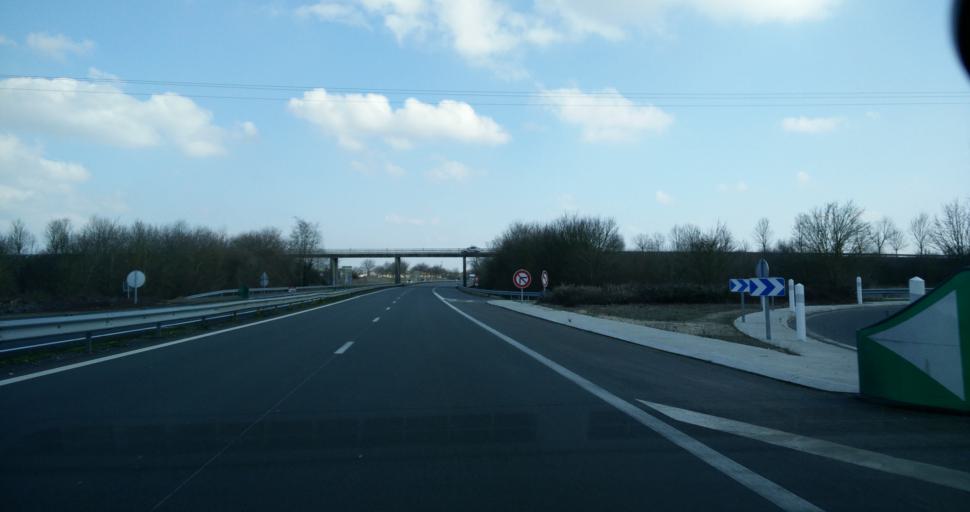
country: FR
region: Poitou-Charentes
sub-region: Departement de la Charente-Maritime
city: Saint-Jean-de-Liversay
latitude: 46.2268
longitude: -0.8807
